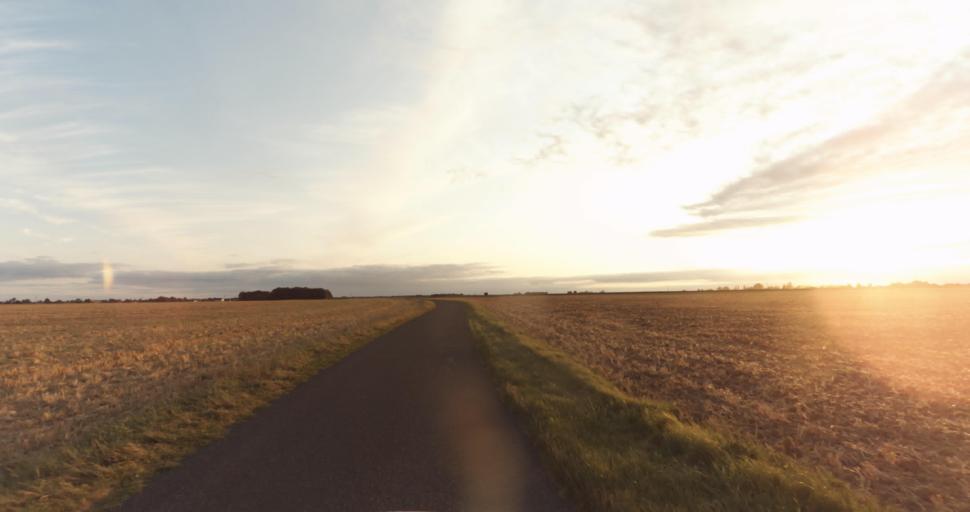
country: FR
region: Haute-Normandie
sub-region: Departement de l'Eure
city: La Madeleine-de-Nonancourt
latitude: 48.8886
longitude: 1.2129
